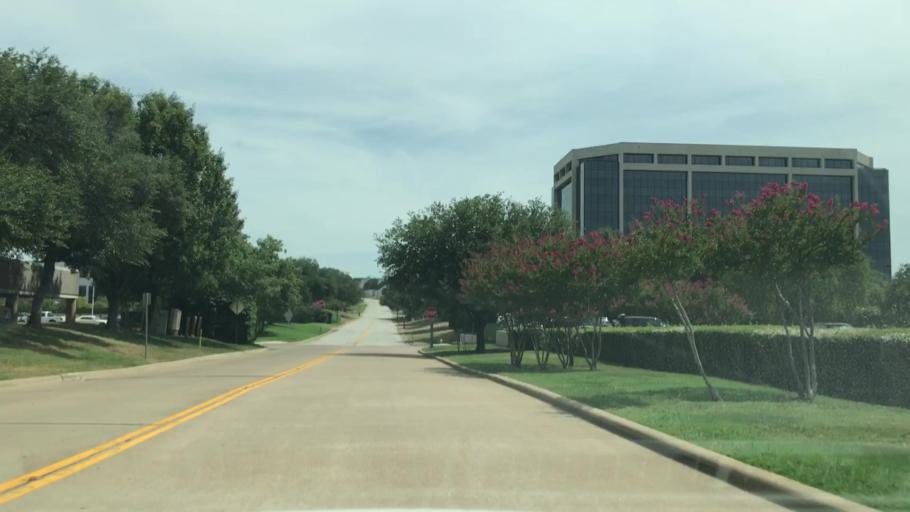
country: US
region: Texas
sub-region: Dallas County
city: Coppell
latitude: 32.8903
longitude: -96.9715
